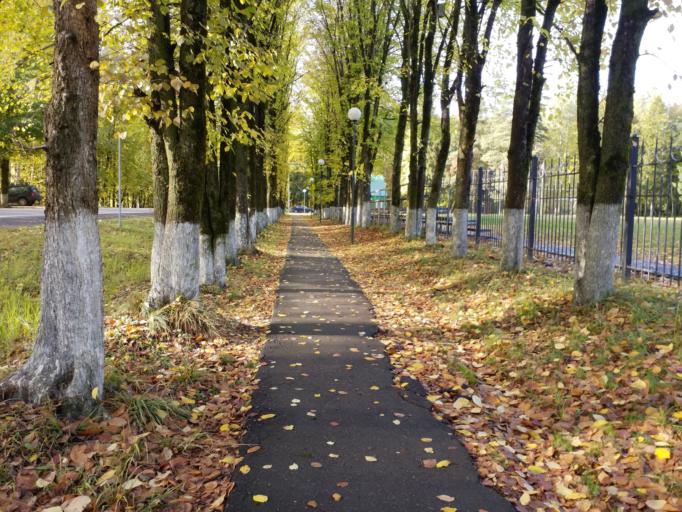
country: RU
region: Moskovskaya
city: Ashukino
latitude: 56.1601
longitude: 37.9518
